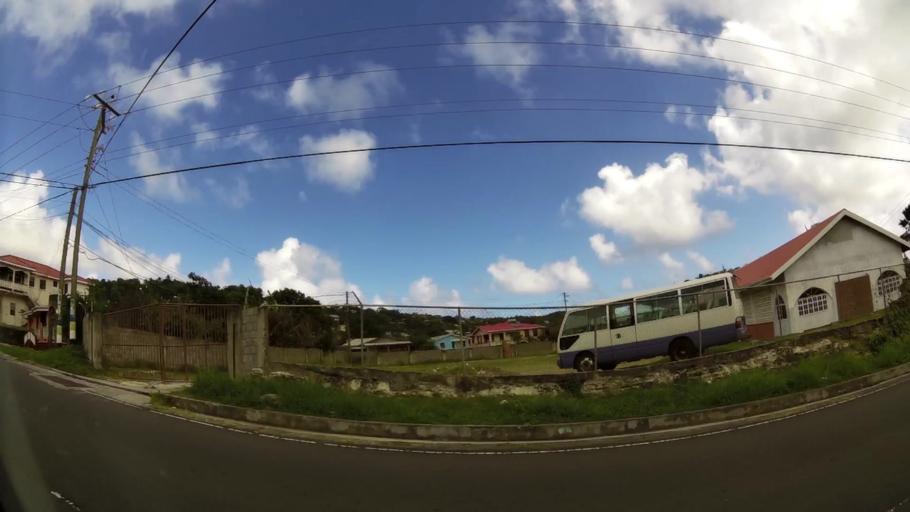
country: LC
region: Dennery Quarter
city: Dennery
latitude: 13.9132
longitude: -60.8949
